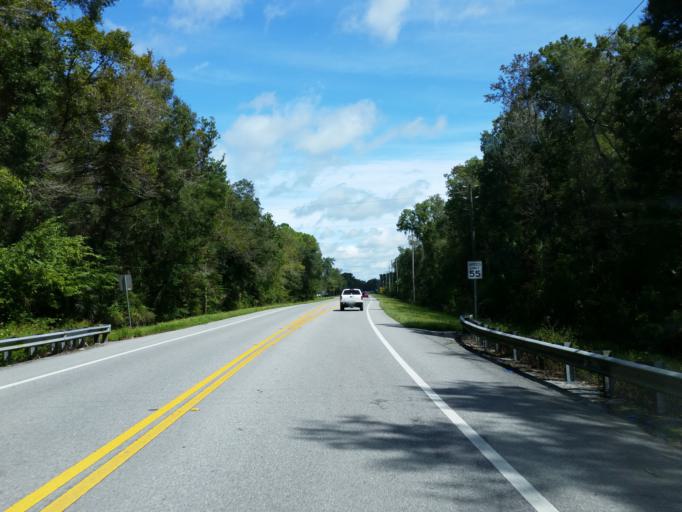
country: US
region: Florida
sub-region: Pasco County
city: Land O' Lakes
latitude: 28.2142
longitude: -82.3906
